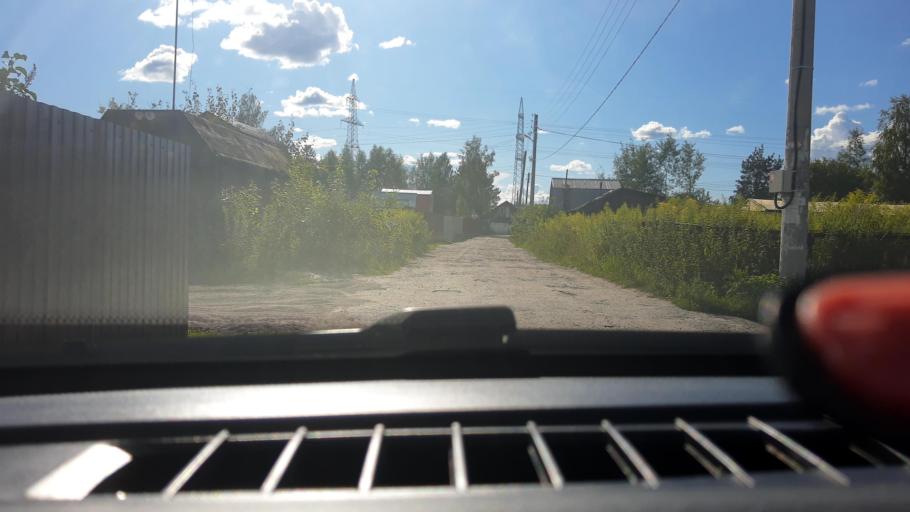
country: RU
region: Nizjnij Novgorod
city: Gorbatovka
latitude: 56.3342
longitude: 43.6691
